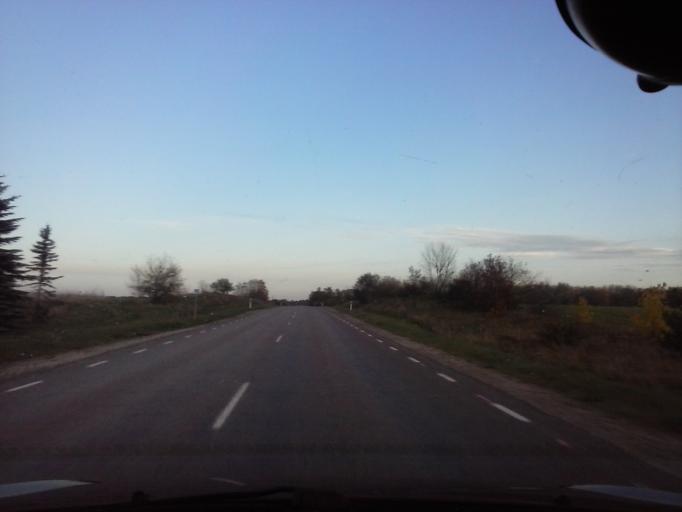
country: EE
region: Harju
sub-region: Nissi vald
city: Turba
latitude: 58.9172
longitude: 24.1726
